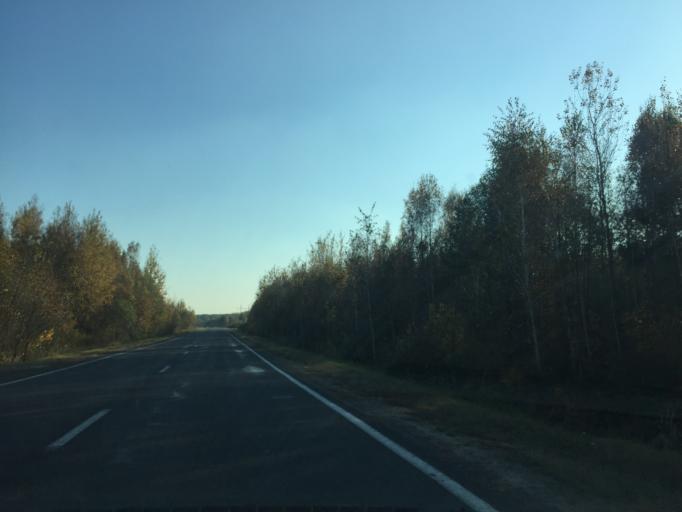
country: BY
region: Gomel
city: Dobrush
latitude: 52.3492
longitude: 31.2293
